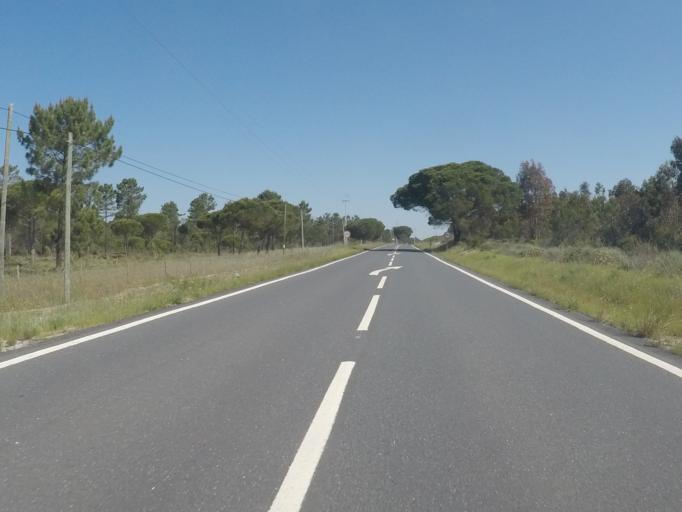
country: PT
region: Setubal
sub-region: Grandola
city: Grandola
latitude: 38.2399
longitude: -8.7372
